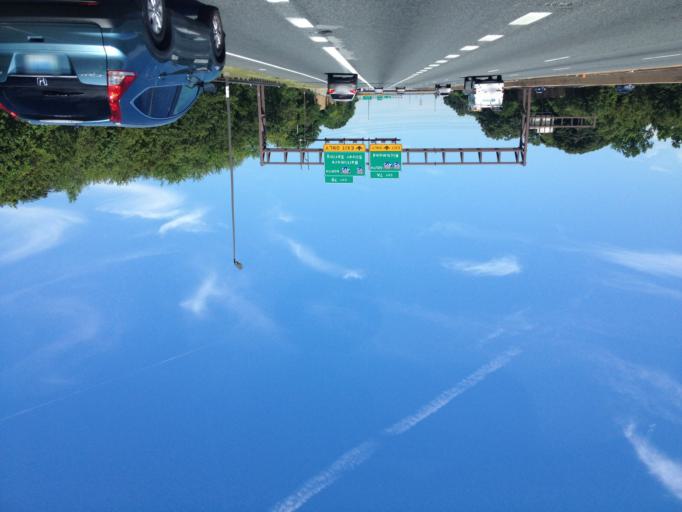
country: US
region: Maryland
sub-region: Prince George's County
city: Springdale
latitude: 38.9465
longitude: -76.8470
